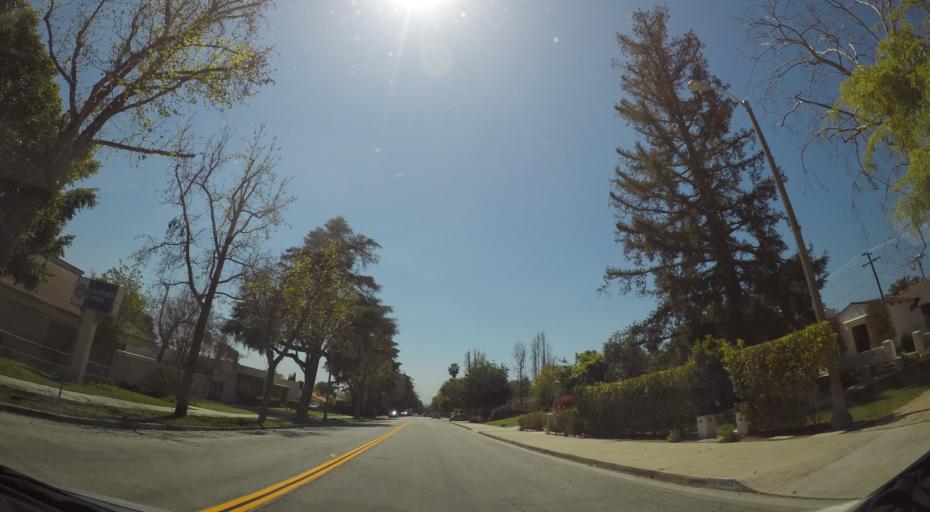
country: US
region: California
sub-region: Los Angeles County
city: Altadena
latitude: 34.1813
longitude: -118.1118
